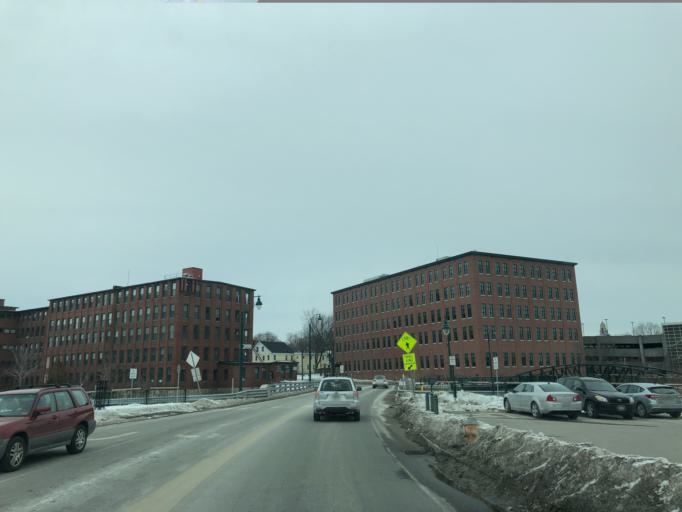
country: US
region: Maine
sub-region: Cumberland County
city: Westbrook
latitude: 43.6770
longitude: -70.3676
